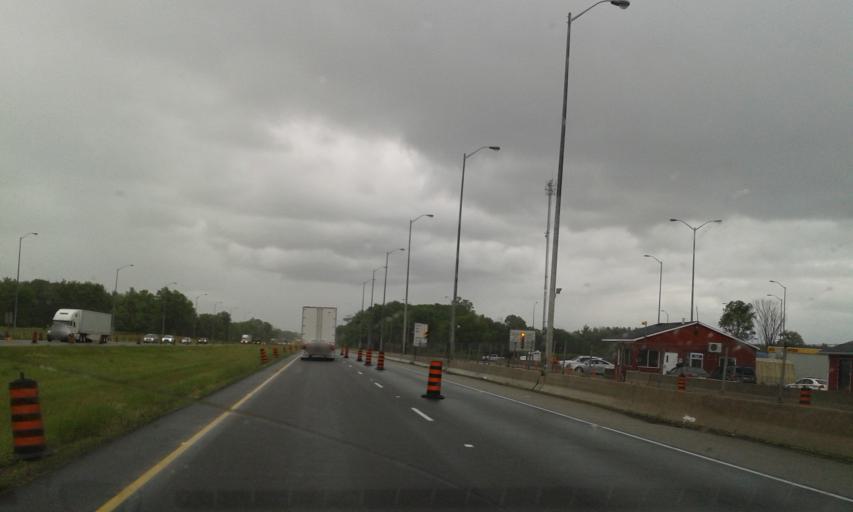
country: CA
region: Ontario
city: Gananoque
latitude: 44.3603
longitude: -76.0818
